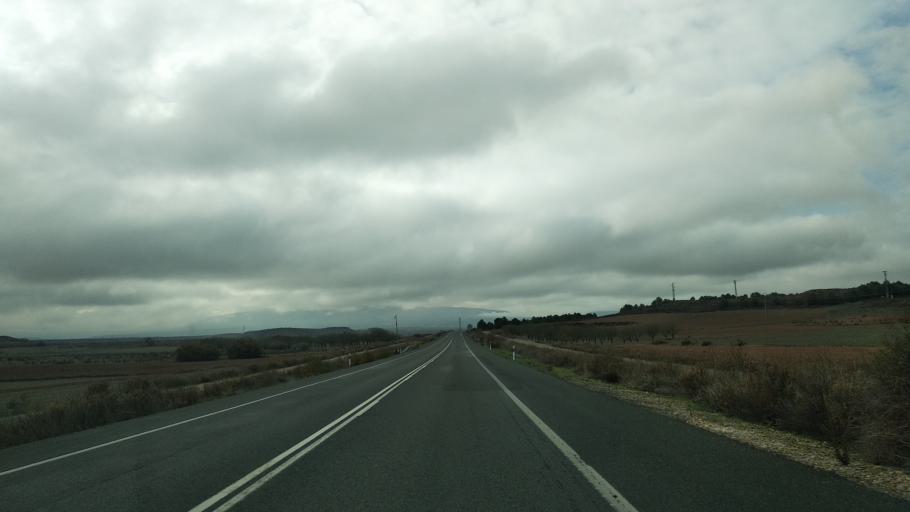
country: ES
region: La Rioja
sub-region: Provincia de La Rioja
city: Pradejon
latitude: 42.3209
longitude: -2.0280
